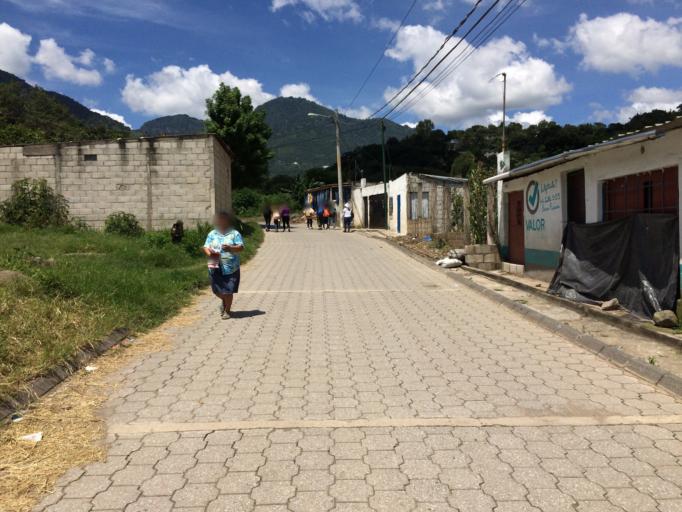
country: GT
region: Guatemala
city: Amatitlan
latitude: 14.4911
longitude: -90.6429
